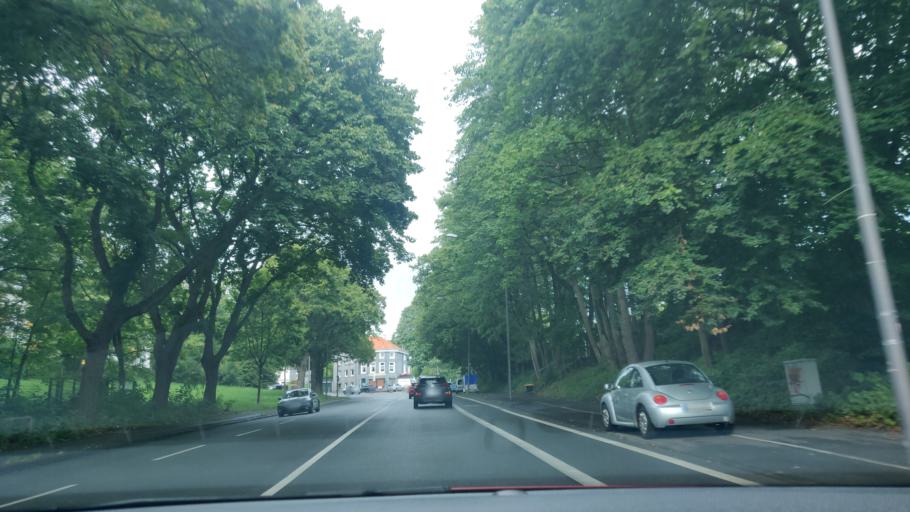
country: DE
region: North Rhine-Westphalia
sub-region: Regierungsbezirk Dusseldorf
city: Wuppertal
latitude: 51.2788
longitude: 7.1243
